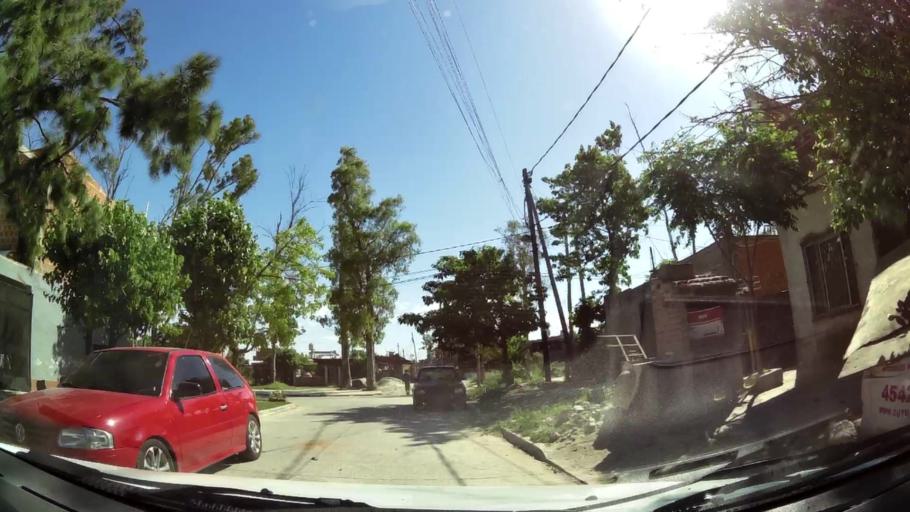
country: AR
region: Buenos Aires
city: Caseros
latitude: -34.5323
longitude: -58.5896
